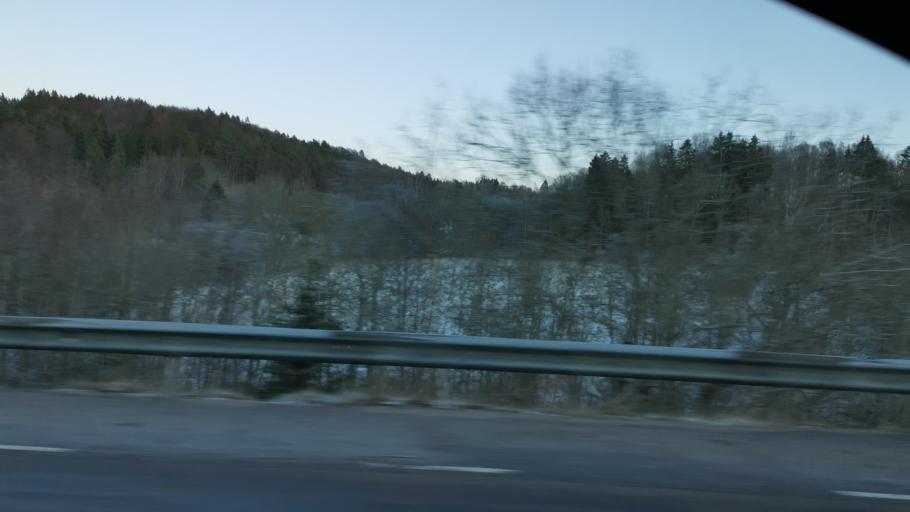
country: SE
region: Vaestra Goetaland
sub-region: Munkedals Kommun
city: Munkedal
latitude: 58.4283
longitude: 11.7225
